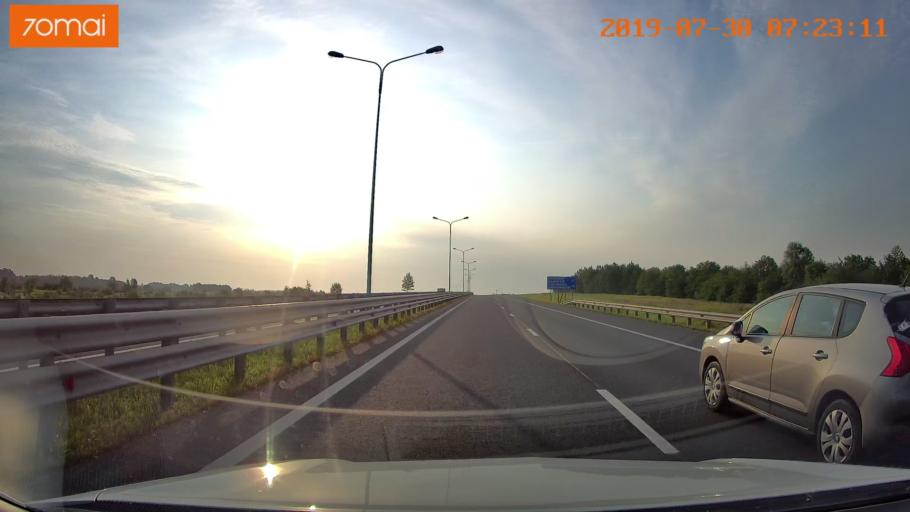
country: RU
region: Kaliningrad
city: Bol'shoe Isakovo
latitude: 54.6919
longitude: 20.7768
